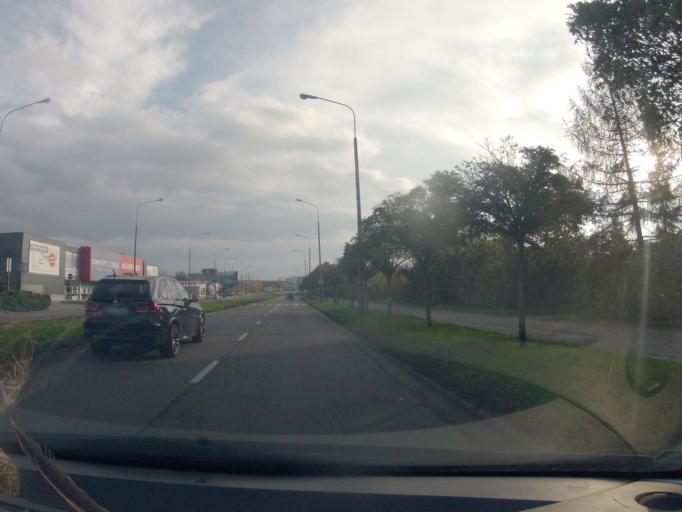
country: PL
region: Opole Voivodeship
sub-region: Powiat opolski
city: Opole
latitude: 50.6713
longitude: 17.9504
